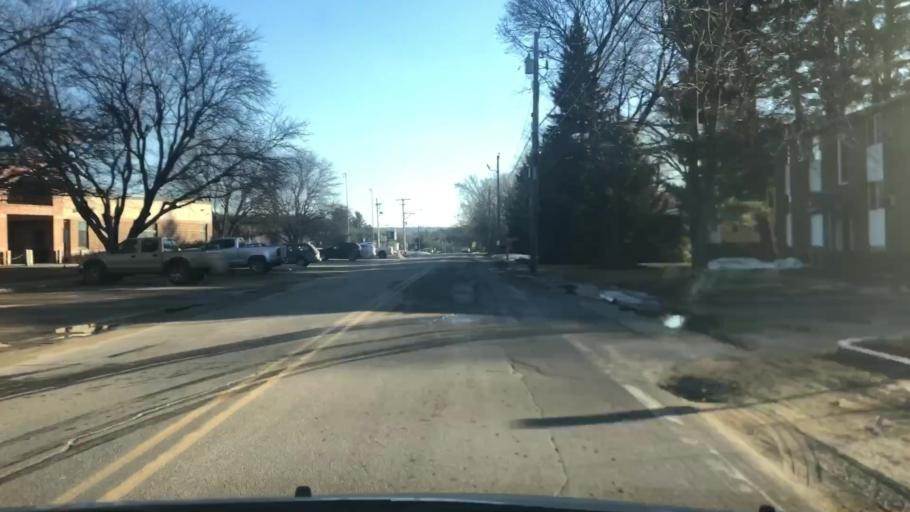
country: US
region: New Hampshire
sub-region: Hillsborough County
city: Milford
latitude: 42.8294
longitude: -71.6608
